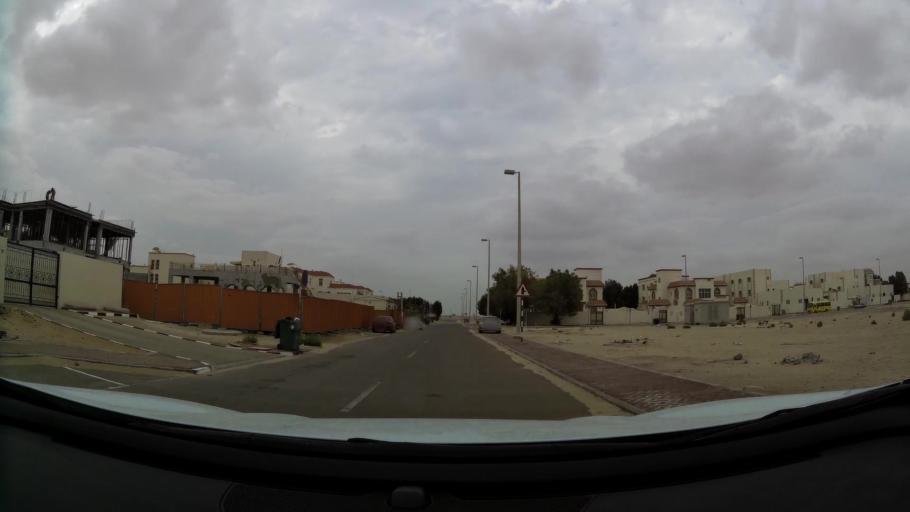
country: AE
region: Abu Dhabi
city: Abu Dhabi
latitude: 24.3775
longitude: 54.6334
